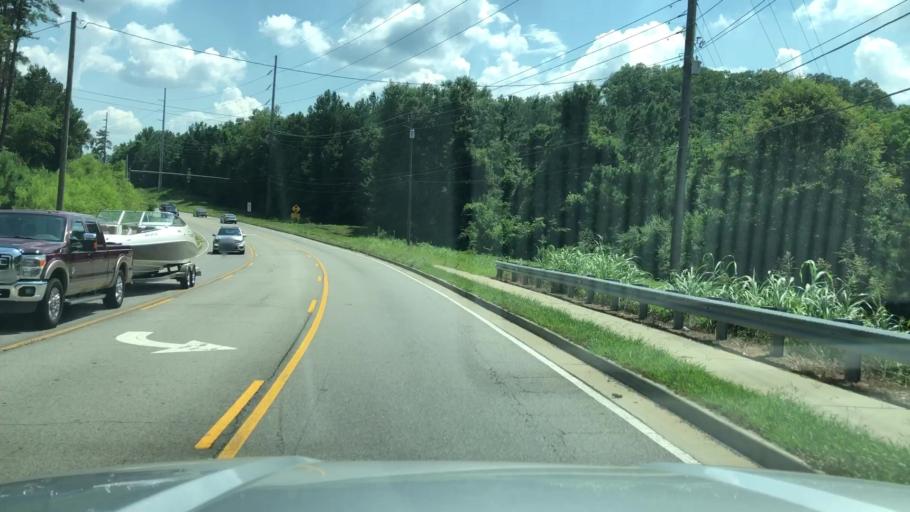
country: US
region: Georgia
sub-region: Cobb County
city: Acworth
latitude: 34.0237
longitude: -84.6993
